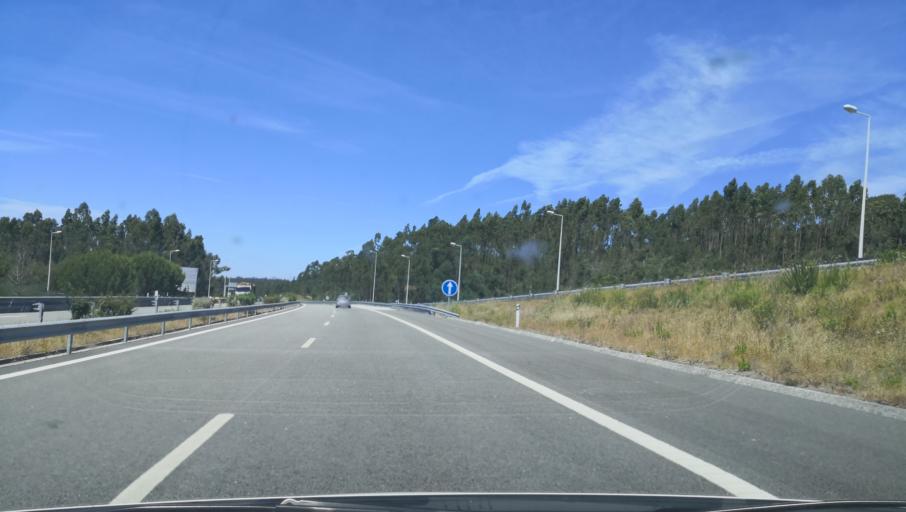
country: PT
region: Coimbra
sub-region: Montemor-O-Velho
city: Montemor-o-Velho
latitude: 40.2041
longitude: -8.6750
